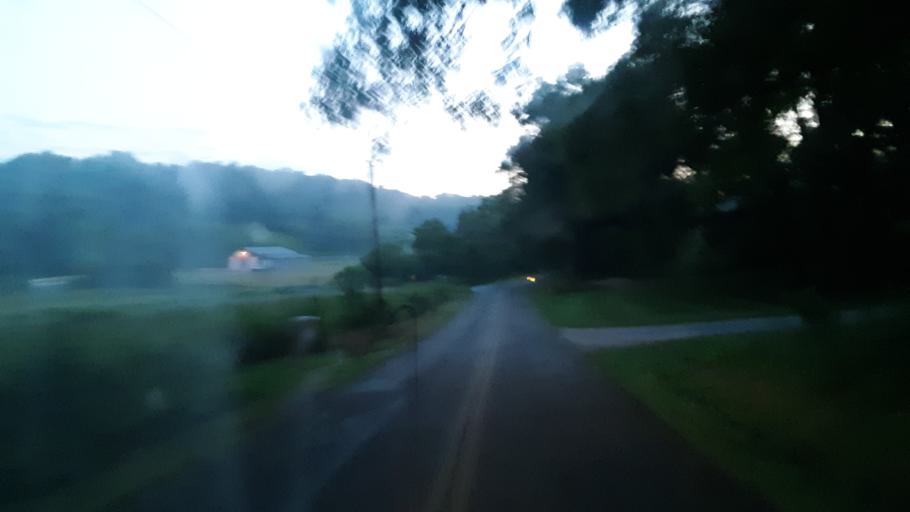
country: US
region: Ohio
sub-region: Carroll County
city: Carrollton
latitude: 40.5848
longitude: -81.1208
